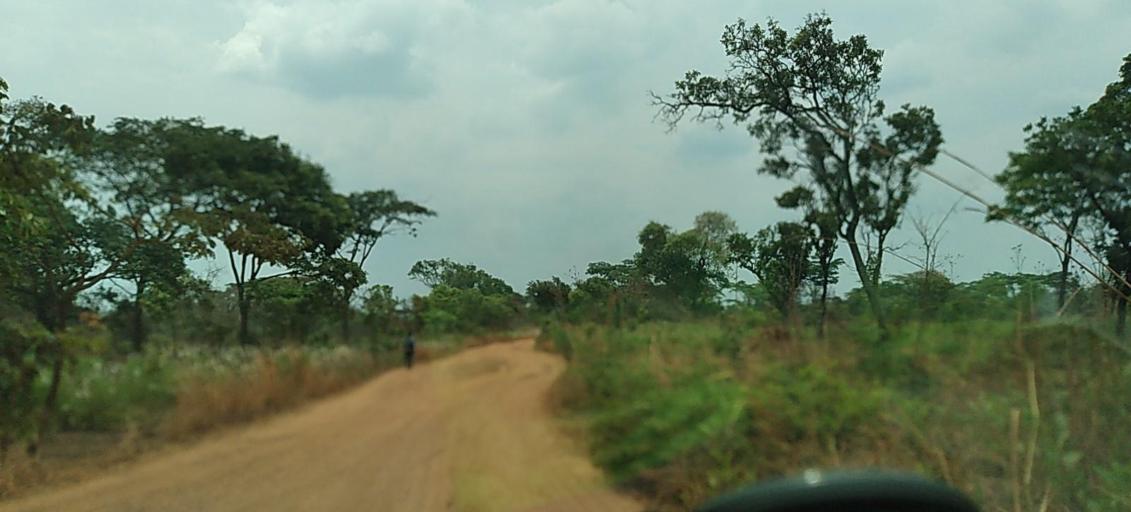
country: ZM
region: North-Western
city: Kansanshi
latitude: -12.0652
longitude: 26.3523
